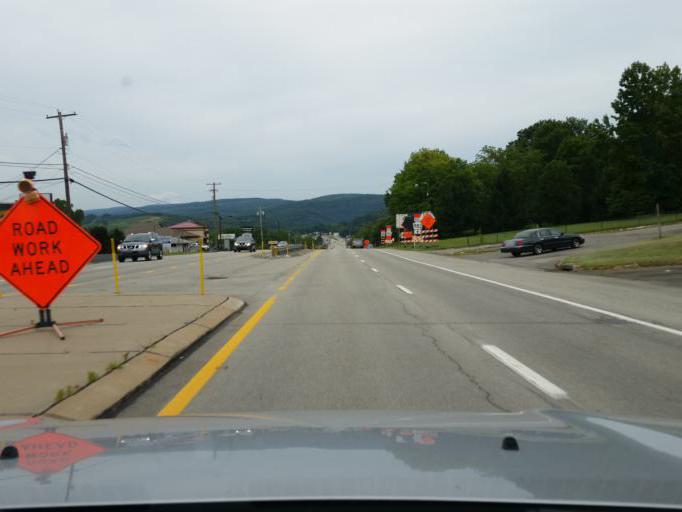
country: US
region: Pennsylvania
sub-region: Westmoreland County
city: Lawson Heights
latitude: 40.2866
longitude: -79.3781
